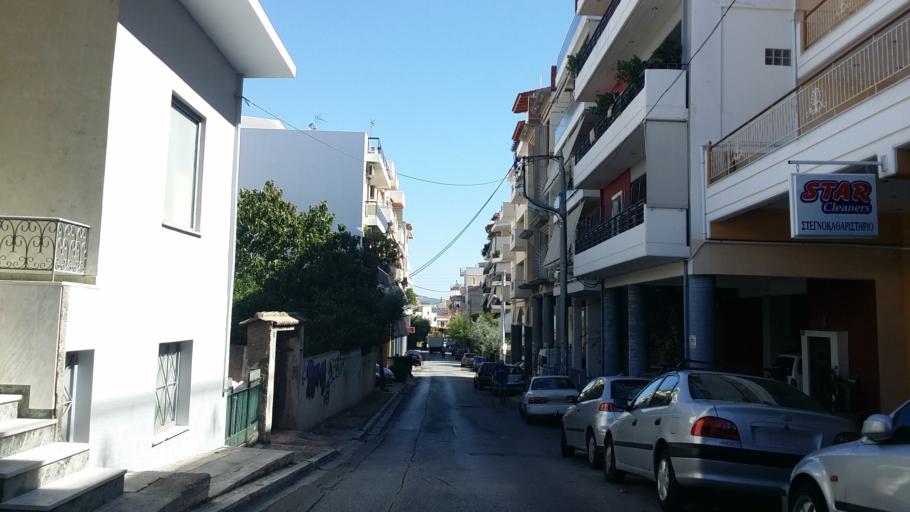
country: GR
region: Attica
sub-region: Nomarchia Athinas
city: Petroupolis
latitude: 38.0286
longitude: 23.6847
